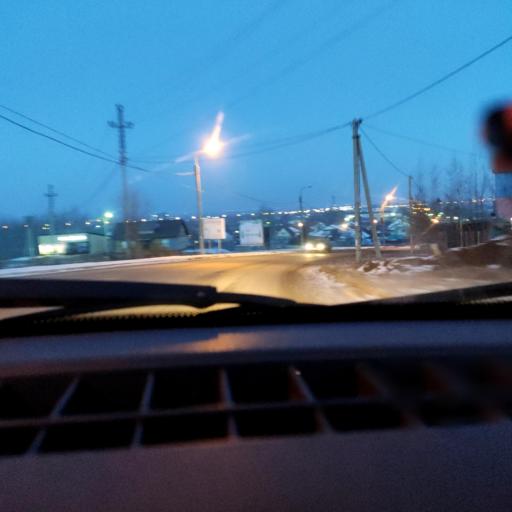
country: RU
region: Bashkortostan
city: Ufa
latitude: 54.6051
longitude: 55.9444
